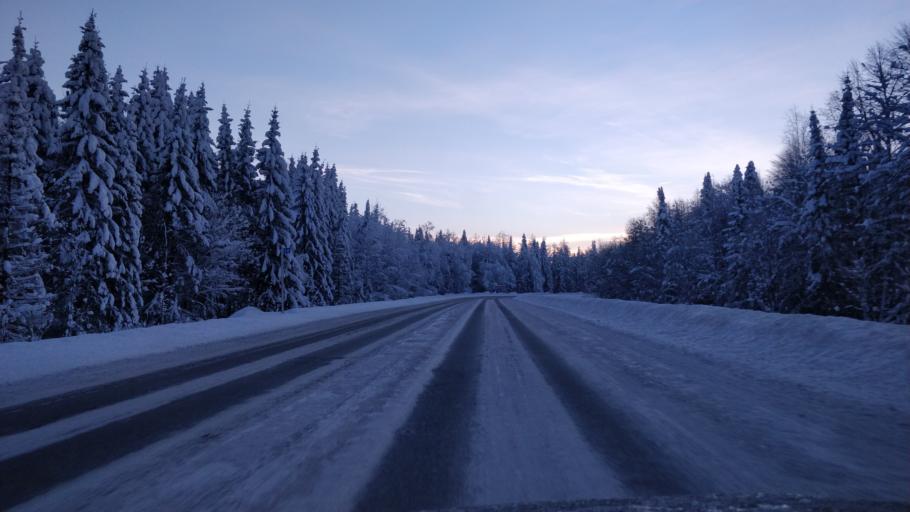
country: RU
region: Perm
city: Polazna
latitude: 58.3012
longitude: 56.6157
